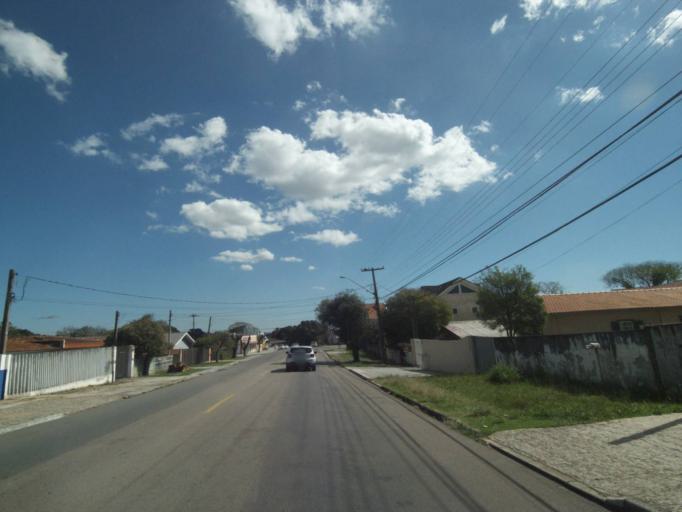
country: BR
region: Parana
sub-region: Curitiba
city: Curitiba
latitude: -25.3823
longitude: -49.2578
